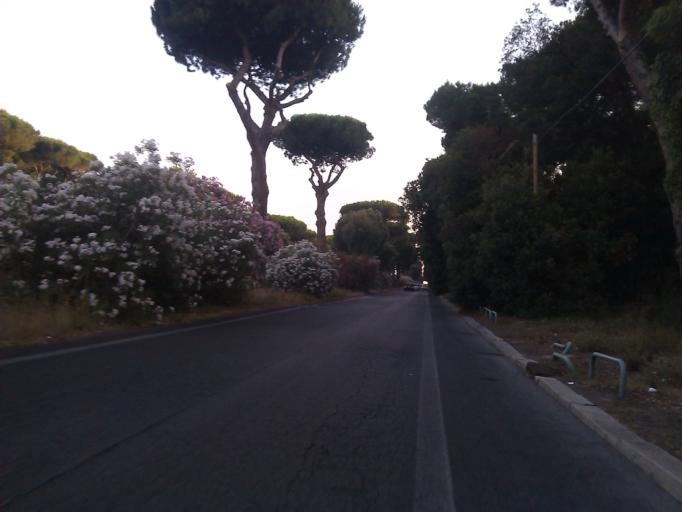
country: IT
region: Latium
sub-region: Citta metropolitana di Roma Capitale
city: Acilia-Castel Fusano-Ostia Antica
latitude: 41.7225
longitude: 12.3273
